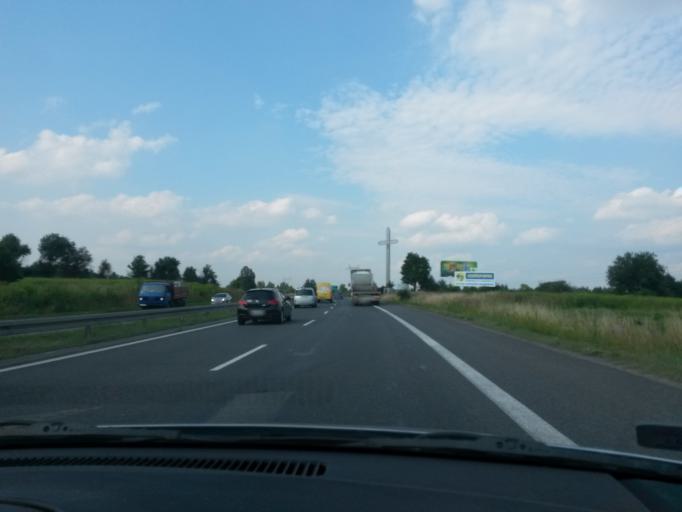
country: PL
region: Silesian Voivodeship
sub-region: Dabrowa Gornicza
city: Dabrowa Gornicza
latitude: 50.2825
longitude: 19.2152
